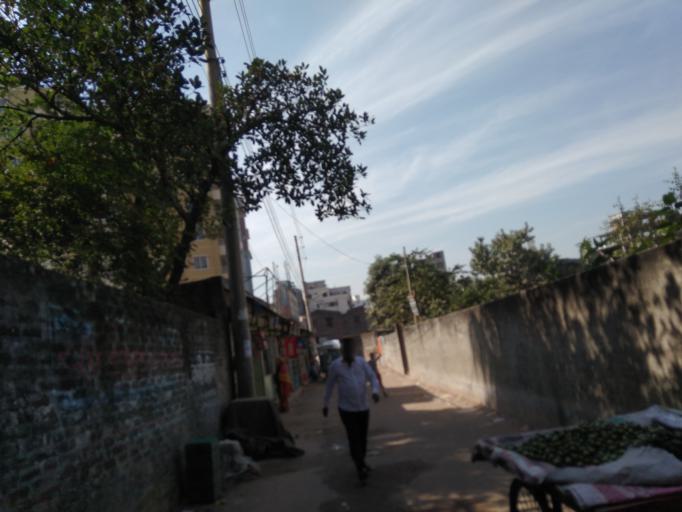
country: BD
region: Dhaka
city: Azimpur
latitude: 23.7753
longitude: 90.3591
